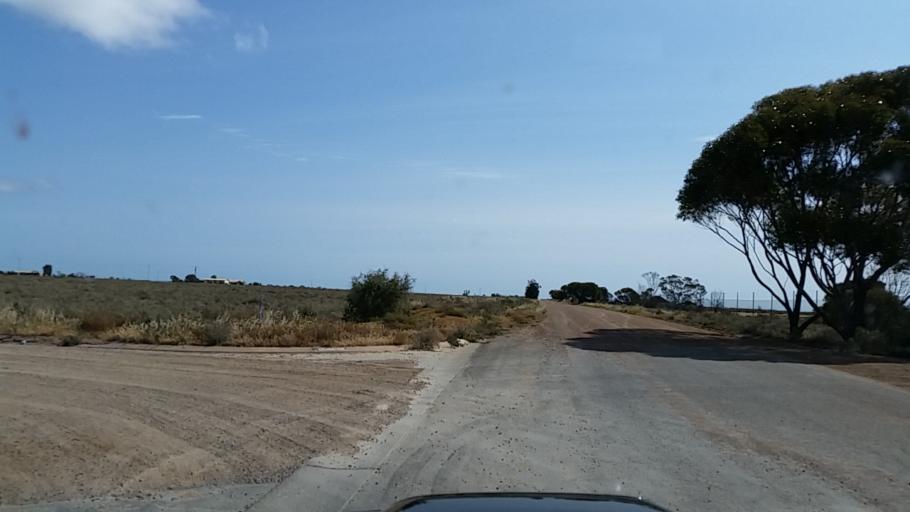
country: AU
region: South Australia
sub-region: Port Pirie City and Dists
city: Port Pirie
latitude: -33.1894
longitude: 137.9878
